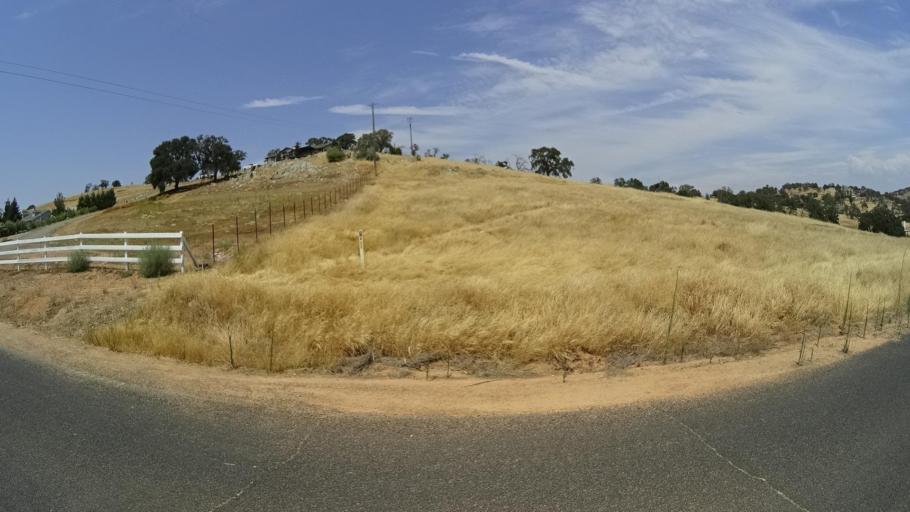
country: US
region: California
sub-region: Tuolumne County
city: Jamestown
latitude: 37.6315
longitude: -120.3342
